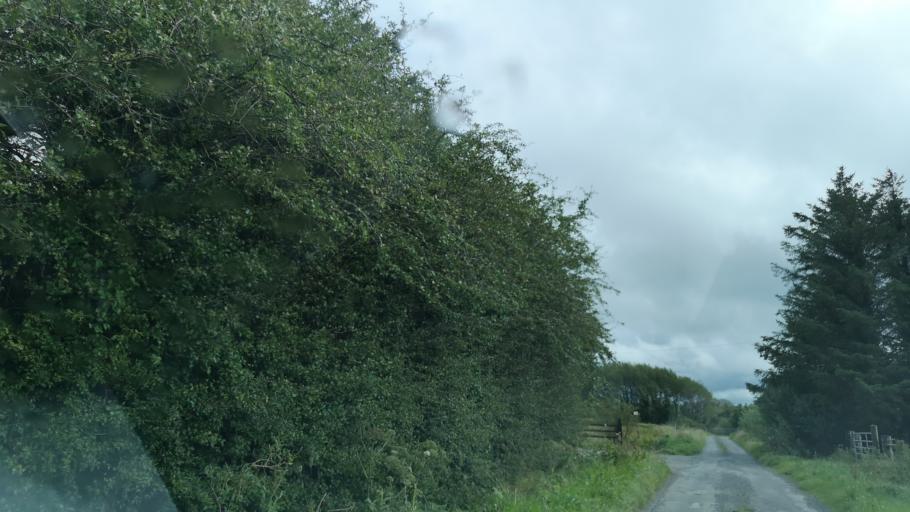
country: IE
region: Connaught
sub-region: County Galway
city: Loughrea
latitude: 53.2996
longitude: -8.5899
